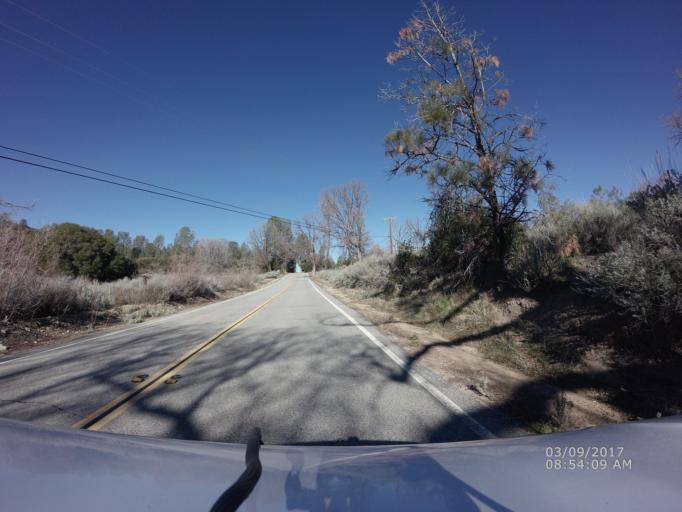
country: US
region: California
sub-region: Los Angeles County
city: Green Valley
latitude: 34.7138
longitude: -118.5632
